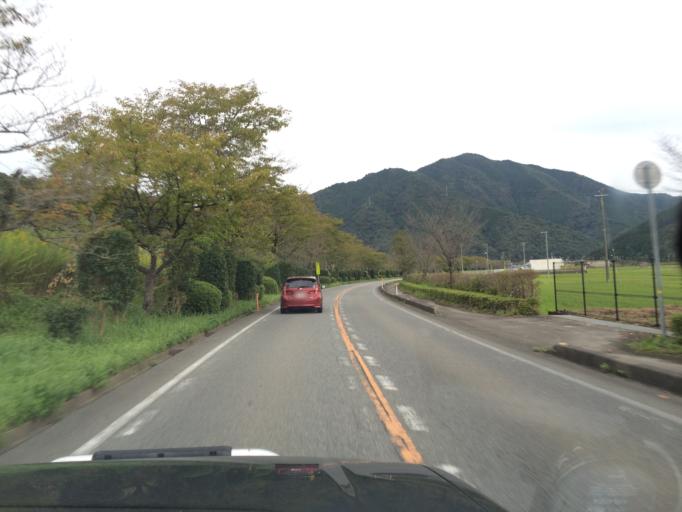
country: JP
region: Hyogo
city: Toyooka
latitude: 35.3761
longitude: 134.8135
